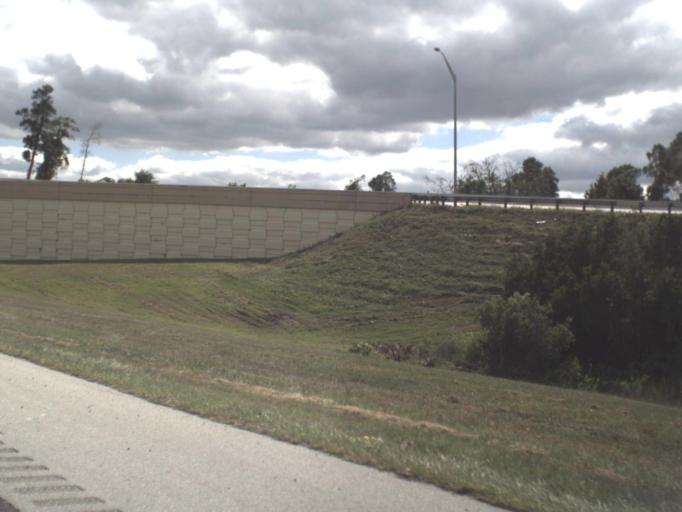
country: US
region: Florida
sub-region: Orange County
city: Gotha
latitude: 28.5352
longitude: -81.5303
